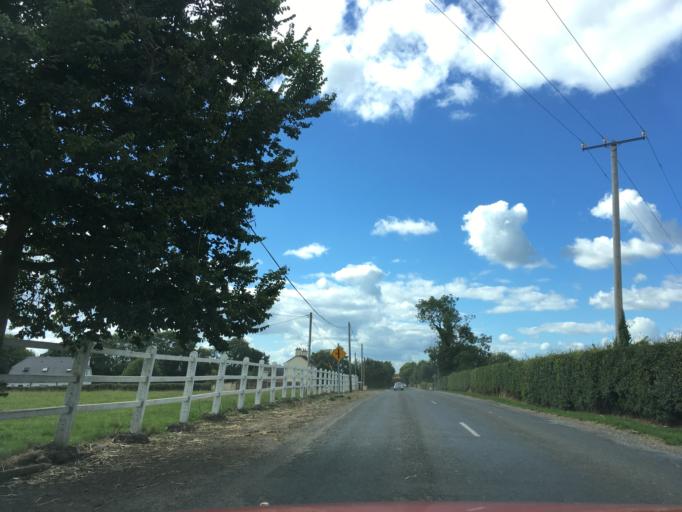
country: IE
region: Munster
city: Cashel
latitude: 52.4888
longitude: -7.9540
